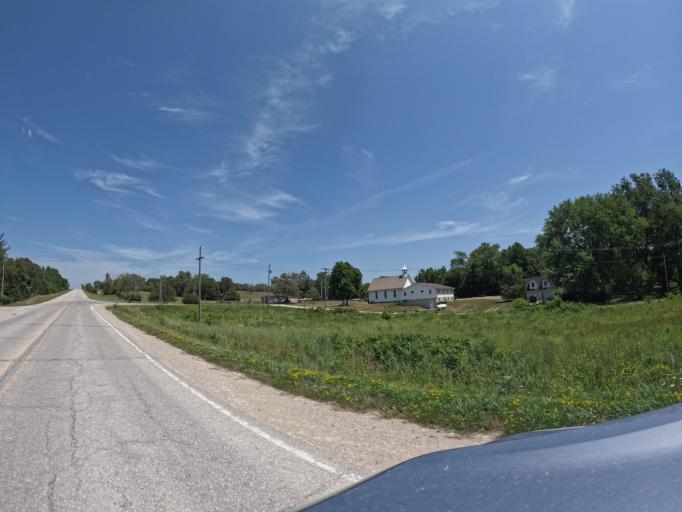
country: US
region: Iowa
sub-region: Henry County
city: Mount Pleasant
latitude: 40.9383
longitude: -91.6175
